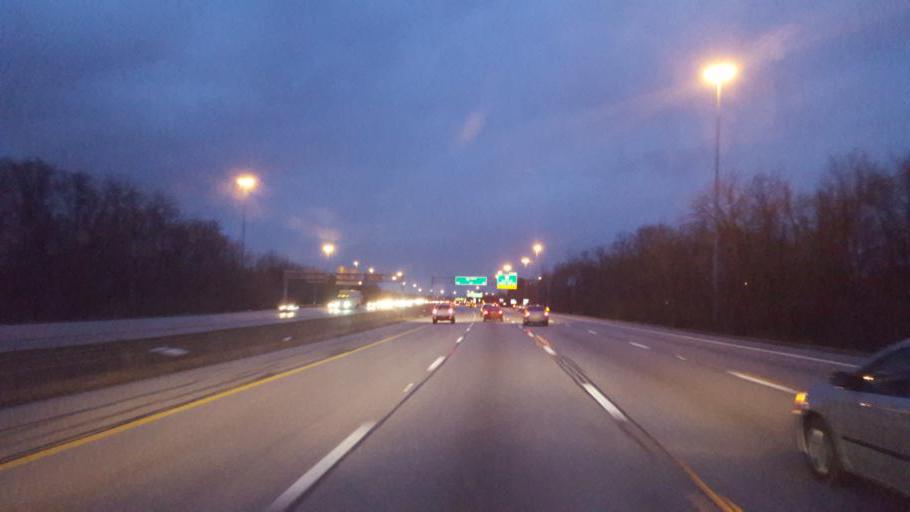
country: US
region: Ohio
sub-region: Franklin County
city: Reynoldsburg
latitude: 39.9708
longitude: -82.8455
